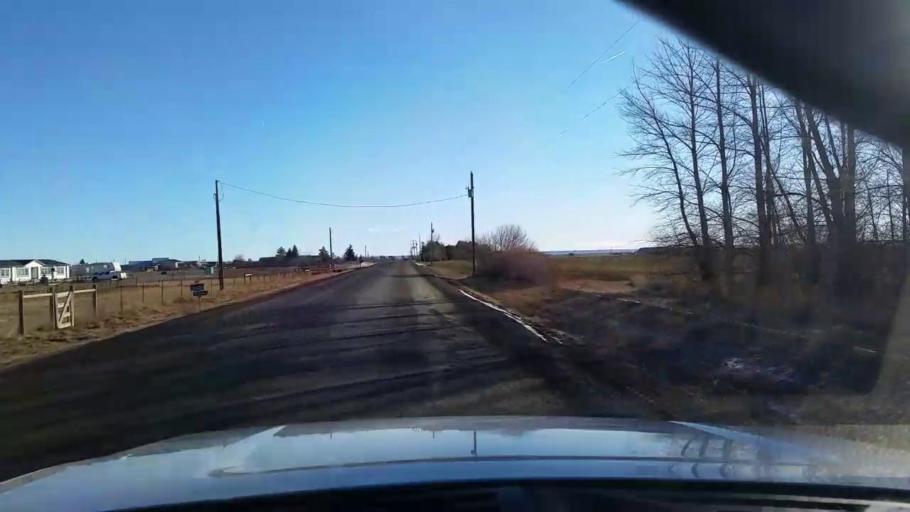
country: US
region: Colorado
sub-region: Larimer County
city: Wellington
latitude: 40.7696
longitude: -105.0830
